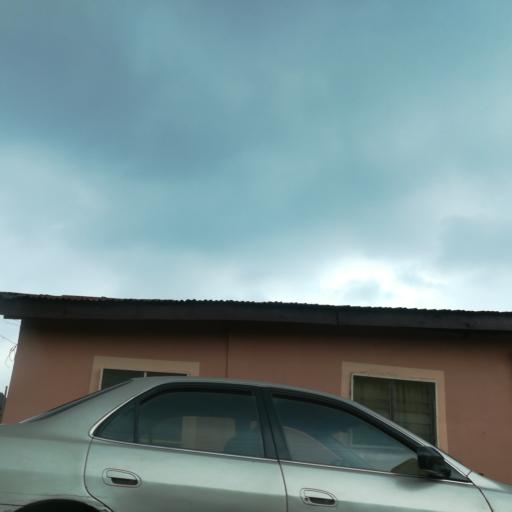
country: NG
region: Lagos
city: Agege
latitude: 6.5876
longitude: 3.3085
